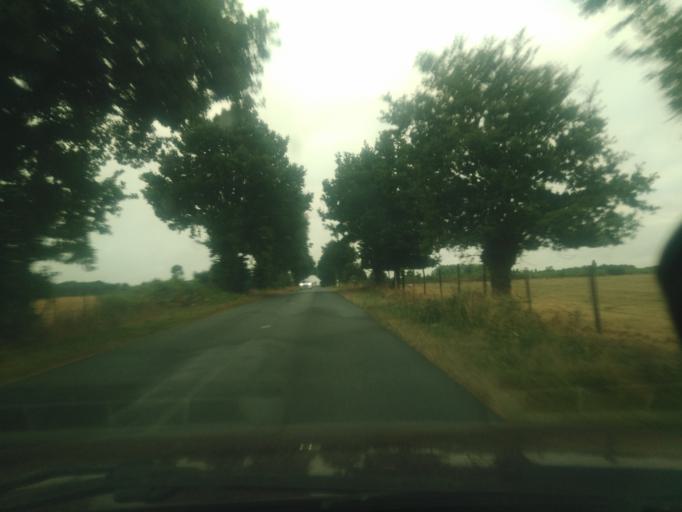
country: FR
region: Pays de la Loire
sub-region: Departement de la Vendee
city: La Ferriere
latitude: 46.7480
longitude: -1.3086
